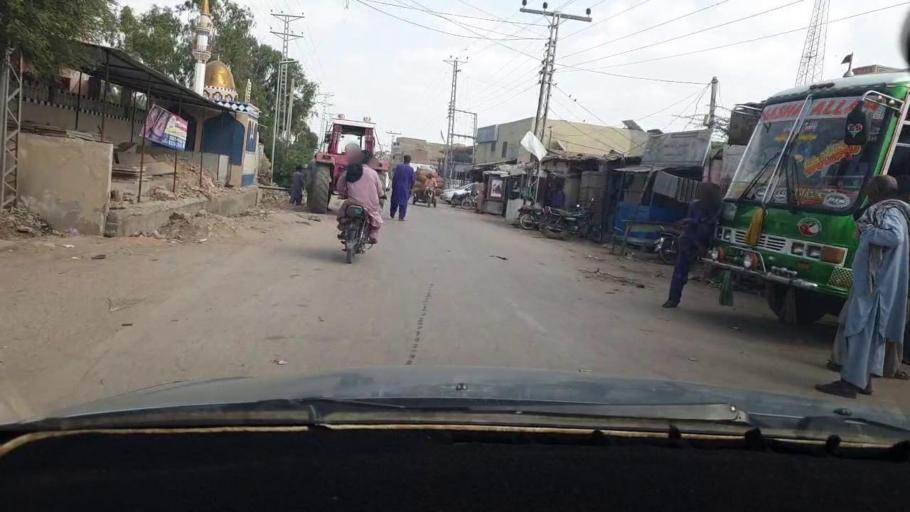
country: PK
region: Sindh
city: Naukot
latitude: 24.8562
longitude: 69.4001
